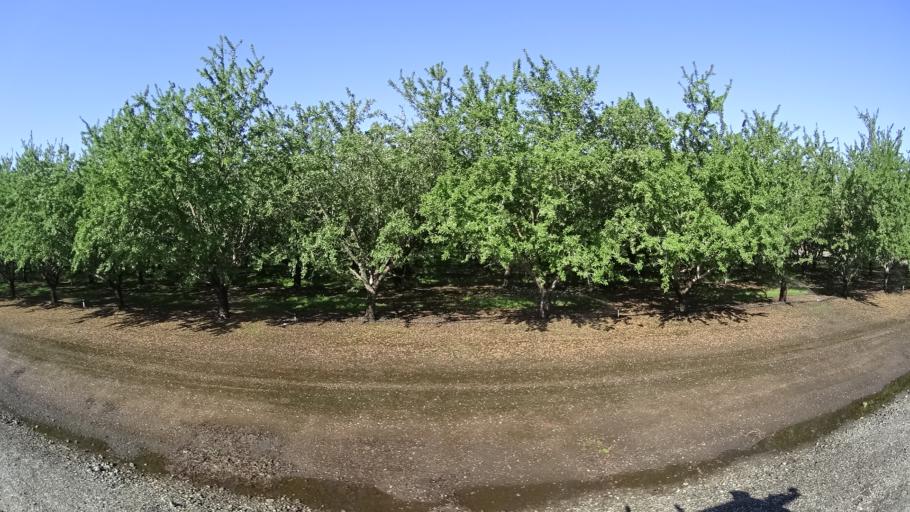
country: US
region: California
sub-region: Glenn County
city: Hamilton City
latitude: 39.7750
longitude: -122.0477
